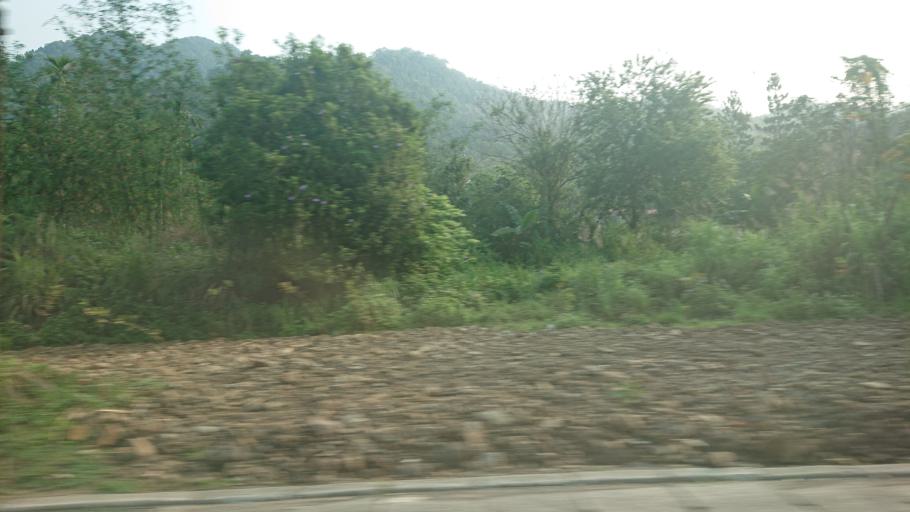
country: TW
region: Taiwan
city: Daxi
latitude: 24.8714
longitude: 121.4056
